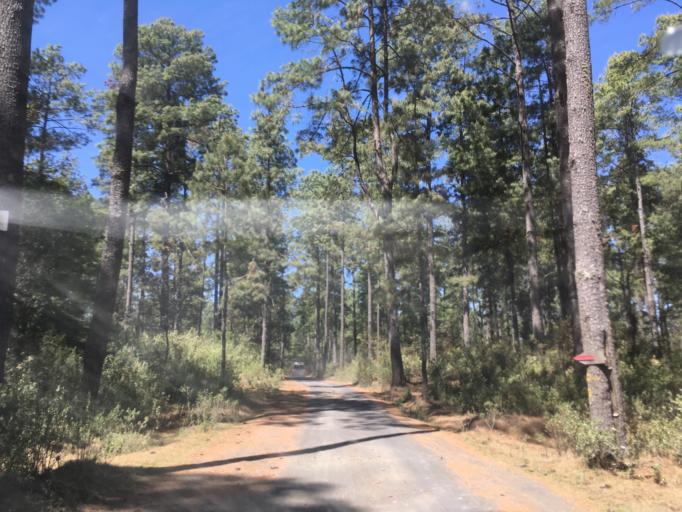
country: MX
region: Michoacan
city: Angahuan
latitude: 19.4639
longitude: -102.2191
